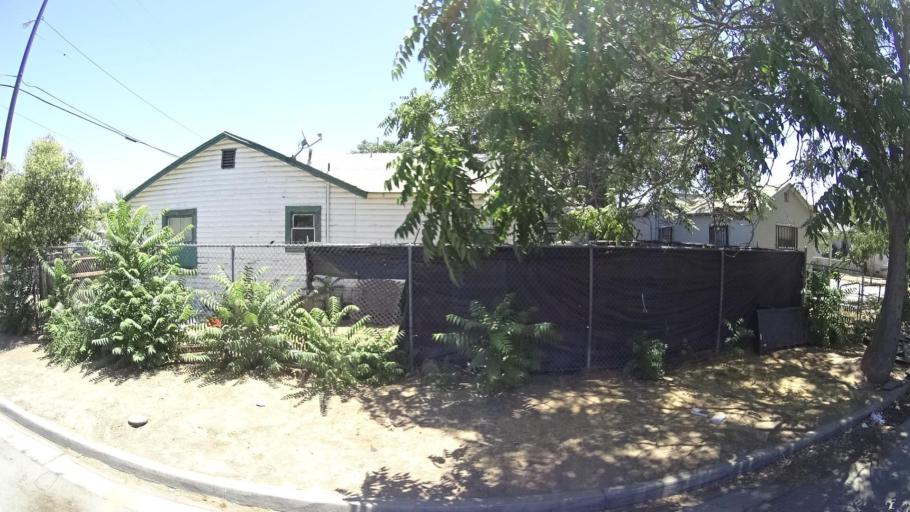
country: US
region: California
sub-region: Fresno County
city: Fresno
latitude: 36.7119
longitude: -119.7559
